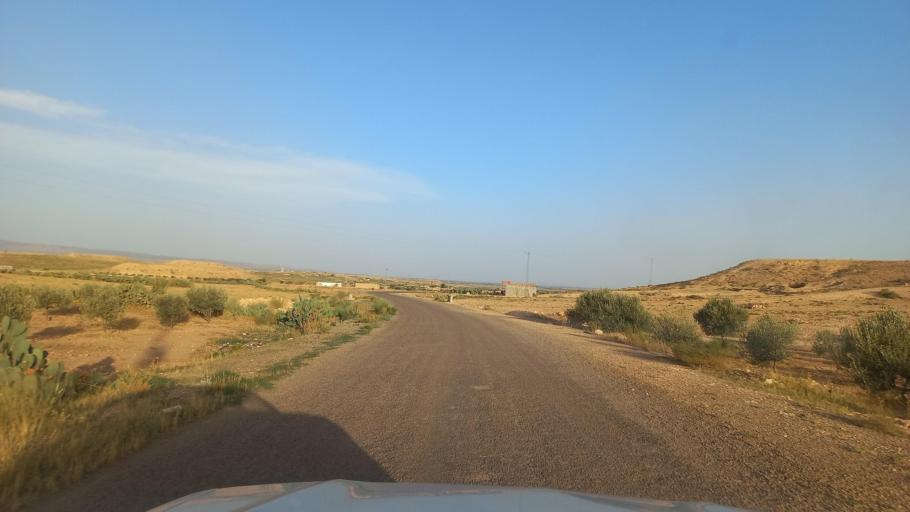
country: TN
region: Al Qasrayn
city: Kasserine
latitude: 35.2746
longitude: 8.9178
